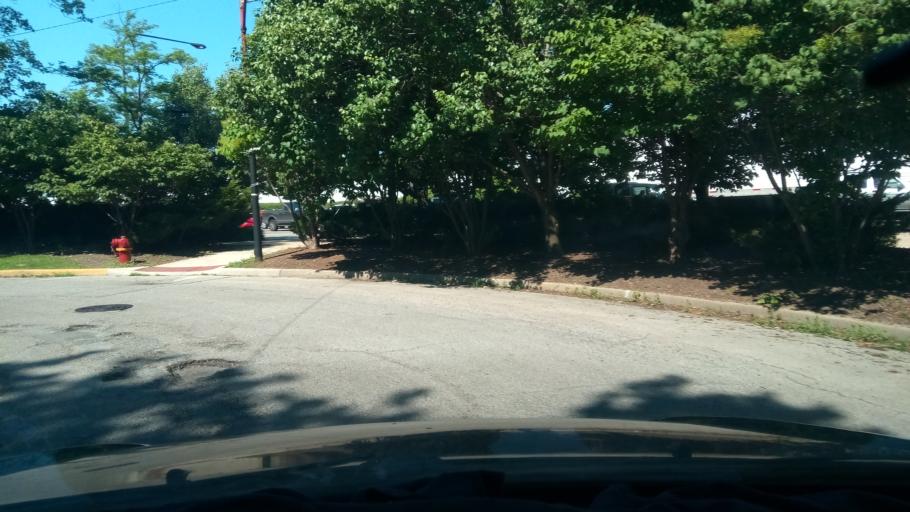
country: US
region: Illinois
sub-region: Cook County
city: Hometown
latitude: 41.7836
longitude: -87.7405
